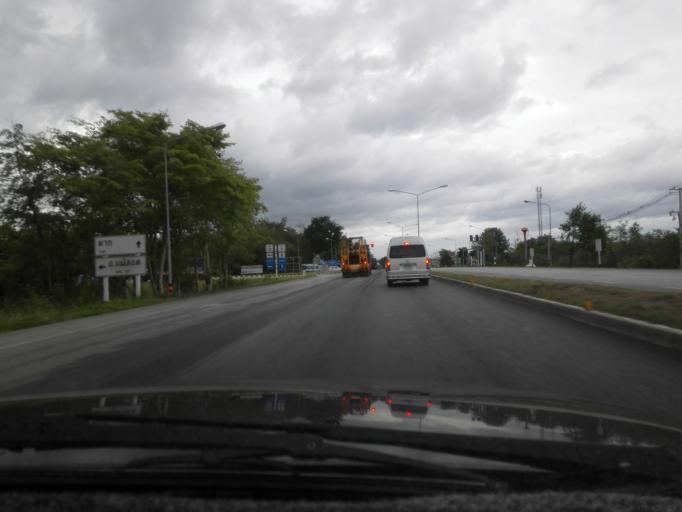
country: TH
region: Tak
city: Tak
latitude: 16.8405
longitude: 99.1143
